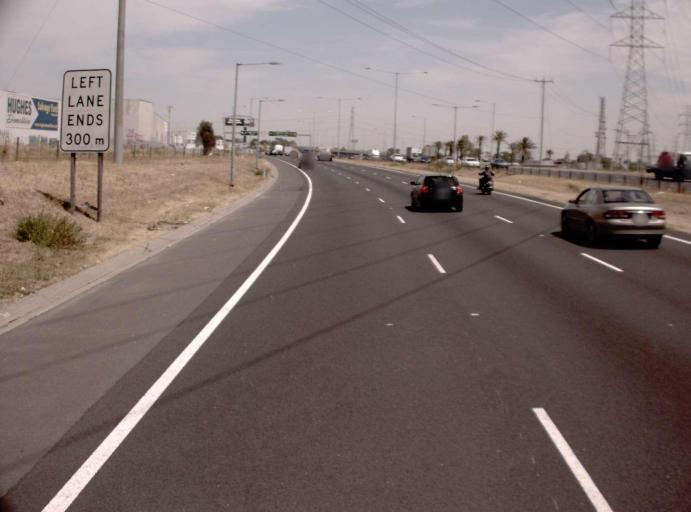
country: AU
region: Victoria
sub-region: Moonee Valley
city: Keilor East
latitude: -37.7334
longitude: 144.8537
